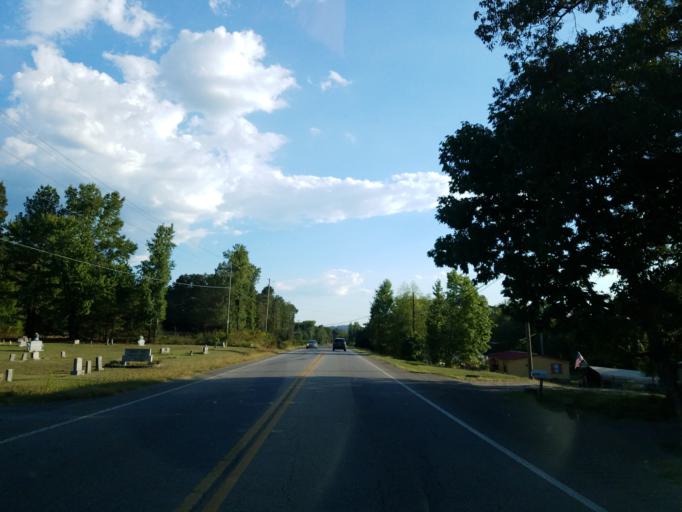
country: US
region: Georgia
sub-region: Murray County
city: Chatsworth
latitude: 34.8614
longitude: -84.7531
